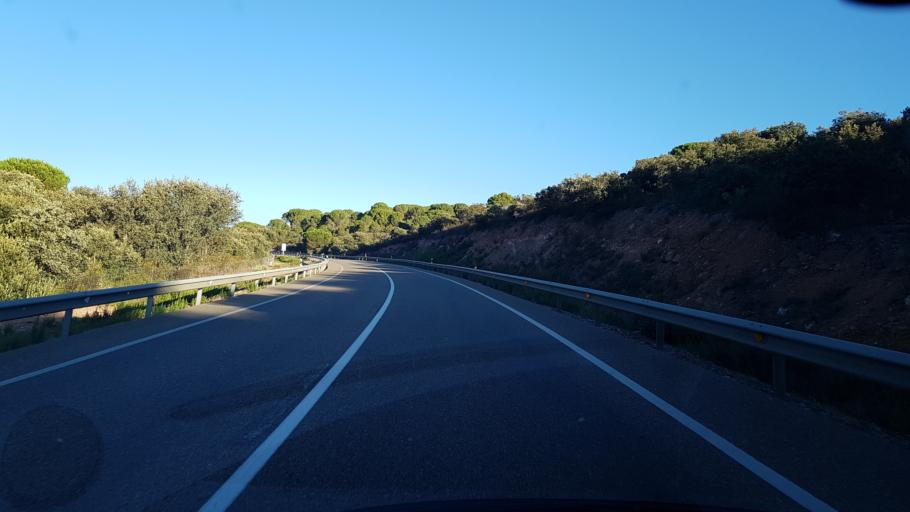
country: ES
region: Castille and Leon
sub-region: Provincia de Zamora
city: Roales
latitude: 41.5381
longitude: -5.8403
